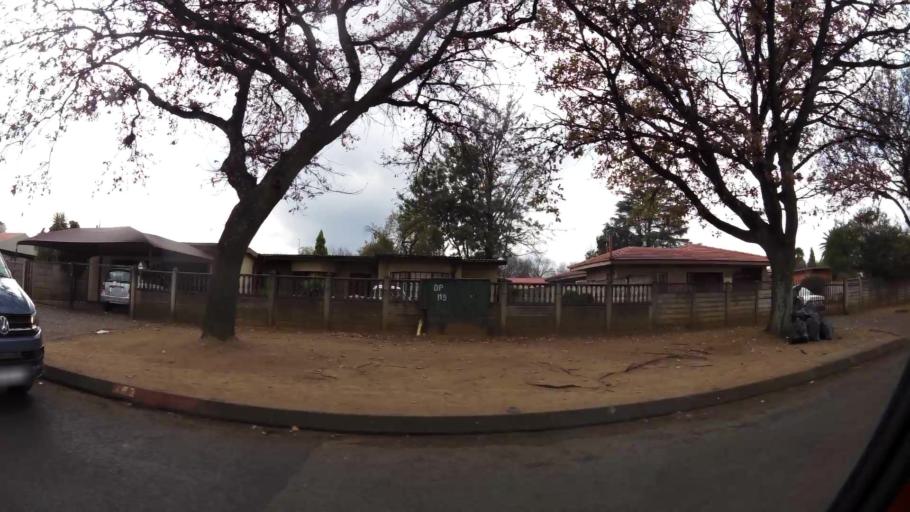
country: ZA
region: Gauteng
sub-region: Sedibeng District Municipality
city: Vanderbijlpark
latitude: -26.7223
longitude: 27.8397
